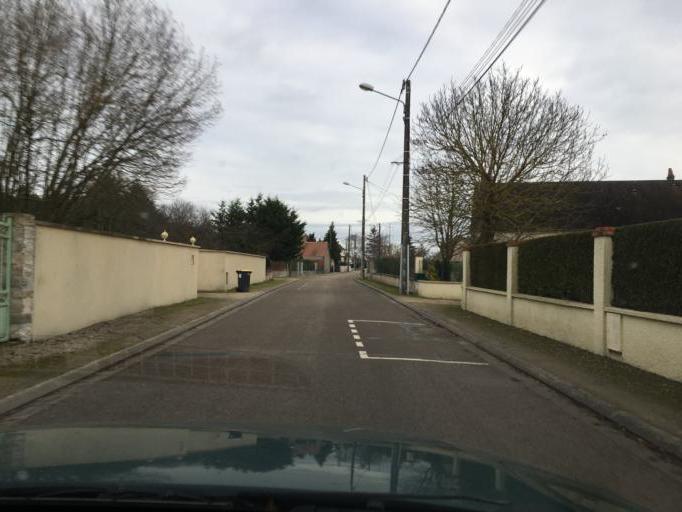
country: FR
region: Centre
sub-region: Departement du Loiret
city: Baule
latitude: 47.8355
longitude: 1.6547
